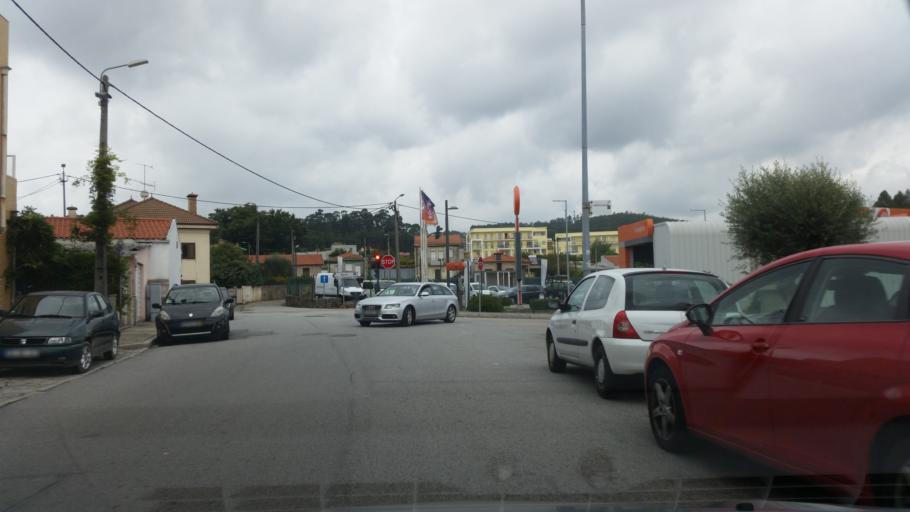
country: PT
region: Porto
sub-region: Valongo
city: Alfena
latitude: 41.2374
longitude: -8.5331
